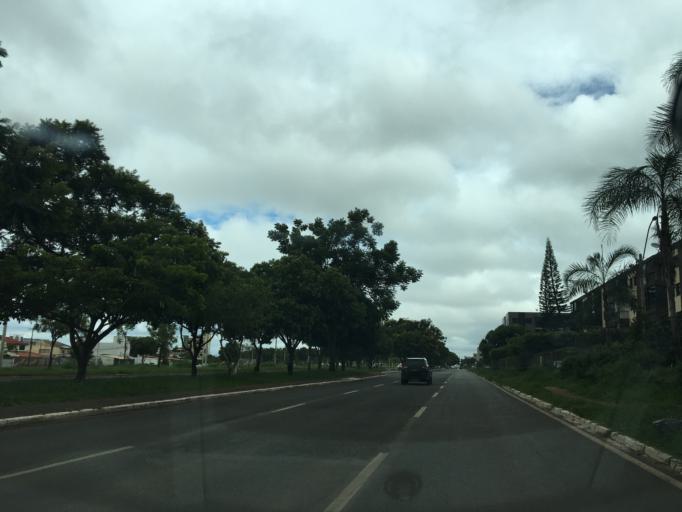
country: BR
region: Federal District
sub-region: Brasilia
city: Brasilia
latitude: -15.8244
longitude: -48.0854
